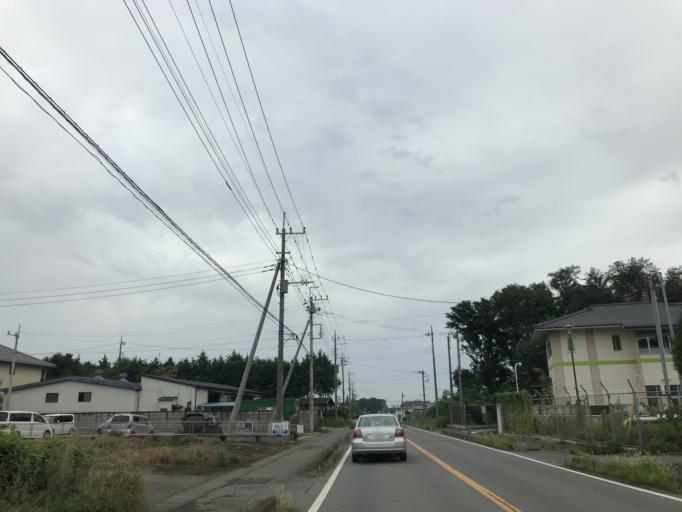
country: JP
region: Ibaraki
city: Sakai
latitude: 36.1231
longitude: 139.7924
